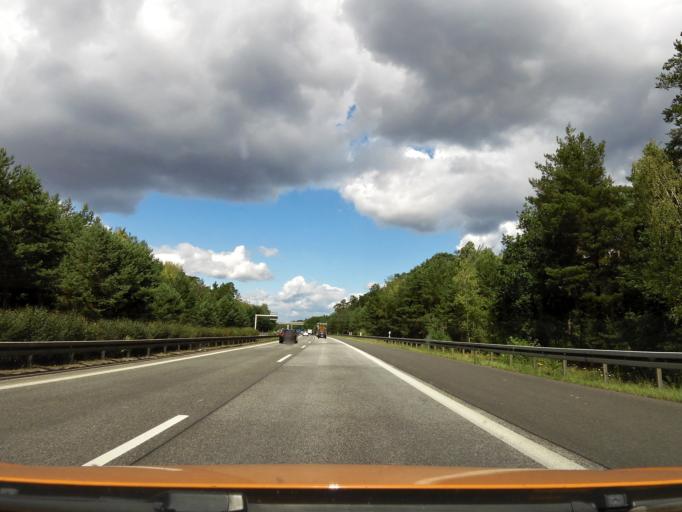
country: DE
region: Brandenburg
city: Hohen Neuendorf
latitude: 52.6625
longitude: 13.2424
